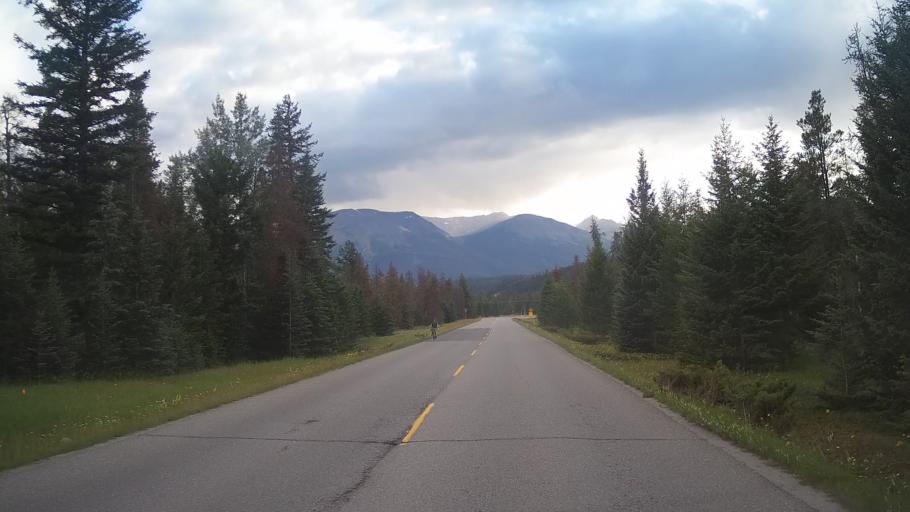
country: CA
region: Alberta
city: Jasper Park Lodge
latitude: 52.9120
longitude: -118.0520
